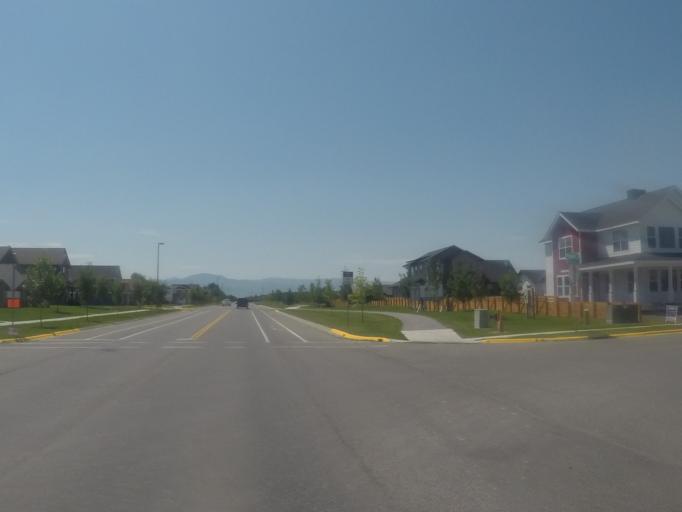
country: US
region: Montana
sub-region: Gallatin County
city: Bozeman
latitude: 45.6897
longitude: -111.0935
